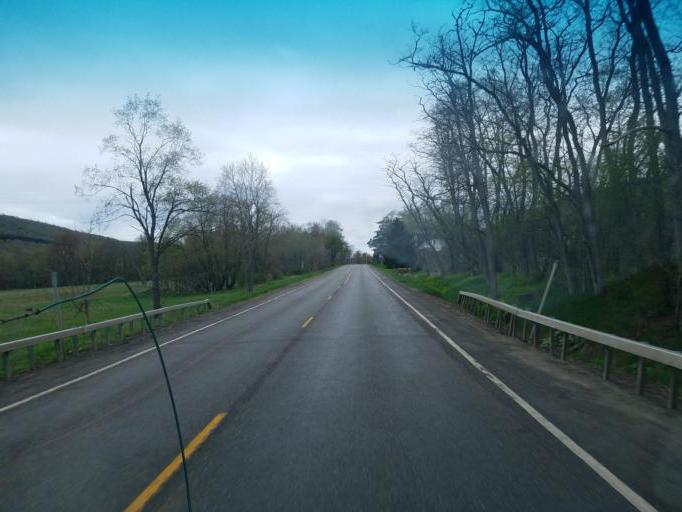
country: US
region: New York
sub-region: Allegany County
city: Andover
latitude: 42.0212
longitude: -77.8207
